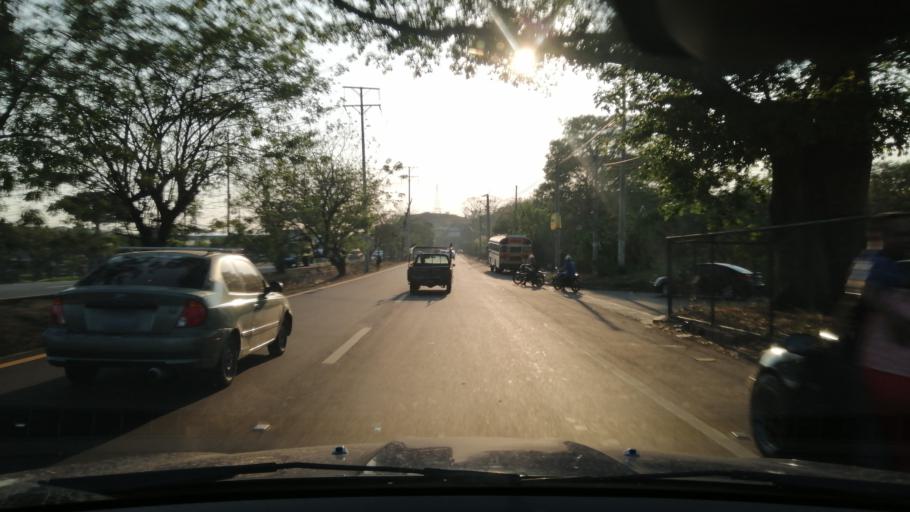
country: SV
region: La Libertad
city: Ciudad Arce
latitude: 13.8151
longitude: -89.4213
